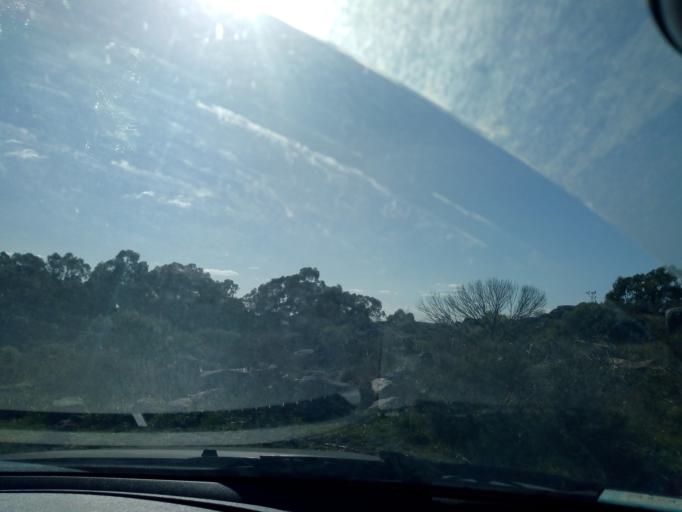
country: AR
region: Buenos Aires
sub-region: Partido de Tandil
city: Tandil
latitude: -37.3640
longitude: -59.1387
